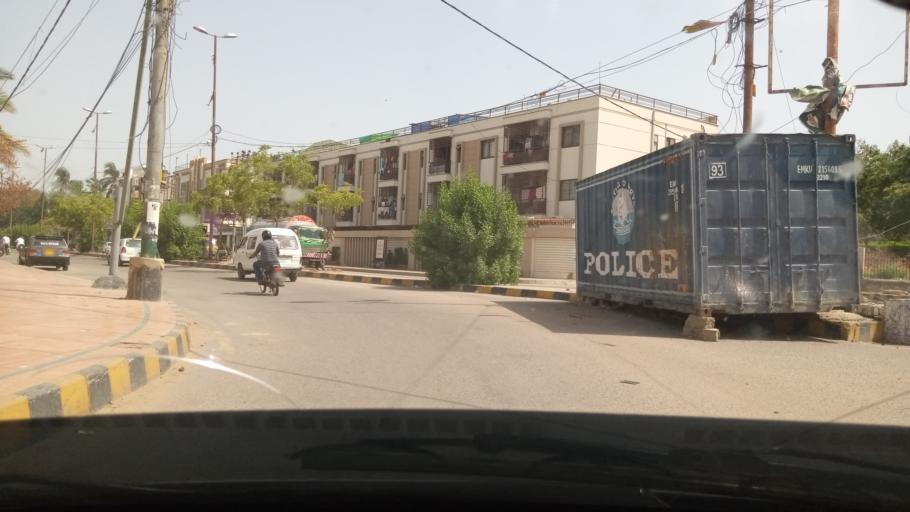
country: PK
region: Sindh
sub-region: Karachi District
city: Karachi
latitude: 24.8769
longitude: 67.0442
